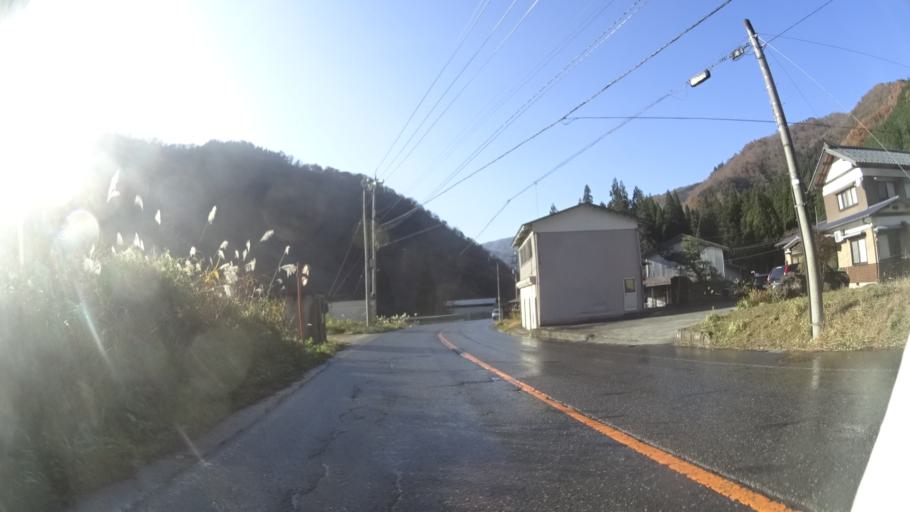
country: JP
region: Fukui
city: Ono
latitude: 35.9007
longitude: 136.6526
